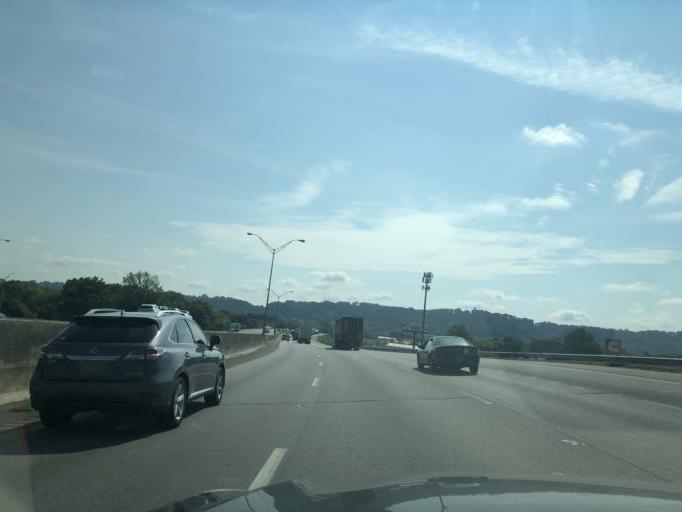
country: US
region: Tennessee
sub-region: Hamilton County
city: Chattanooga
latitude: 35.0192
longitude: -85.2931
